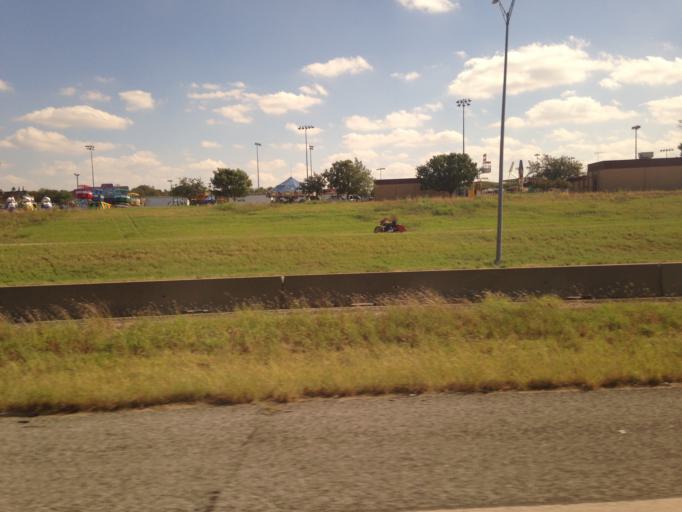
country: US
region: Texas
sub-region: Tarrant County
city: Sansom Park
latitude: 32.8178
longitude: -97.4044
